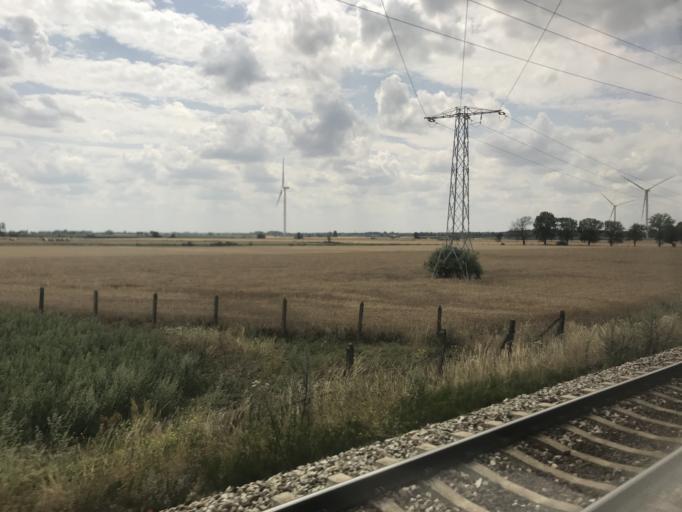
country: PL
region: Greater Poland Voivodeship
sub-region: Powiat poznanski
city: Buk
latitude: 52.3304
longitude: 16.4776
